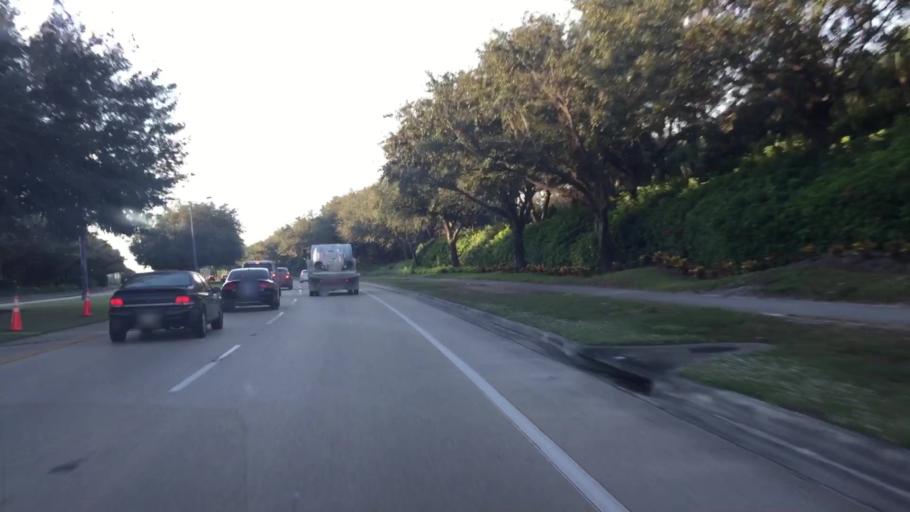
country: US
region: Florida
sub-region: Lee County
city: Three Oaks
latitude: 26.4782
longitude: -81.7867
